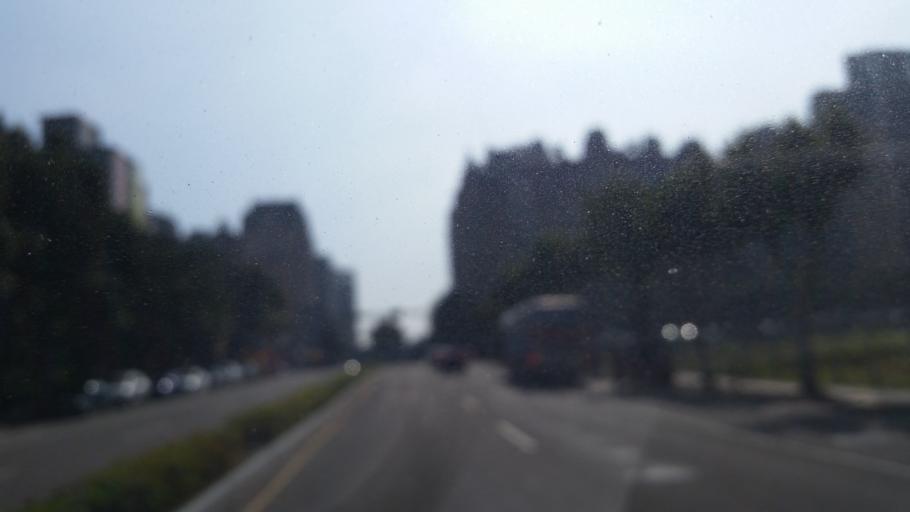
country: TW
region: Taiwan
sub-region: Taoyuan
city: Taoyuan
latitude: 25.0726
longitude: 121.3679
